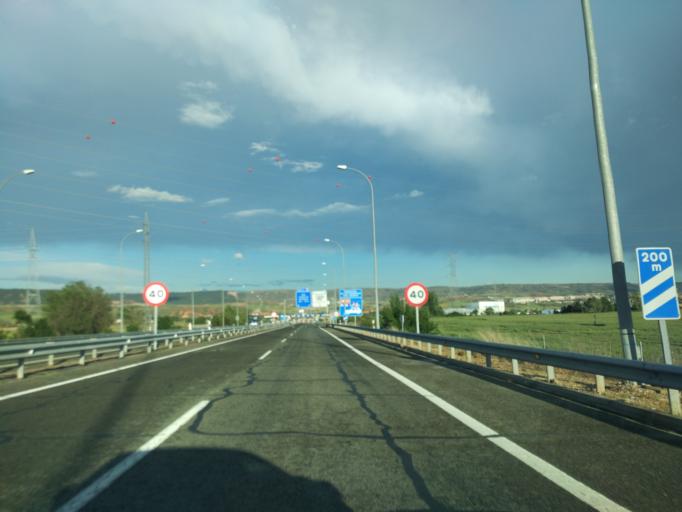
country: ES
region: Castille-La Mancha
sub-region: Provincia de Guadalajara
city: Marchamalo
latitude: 40.6777
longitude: -3.1909
